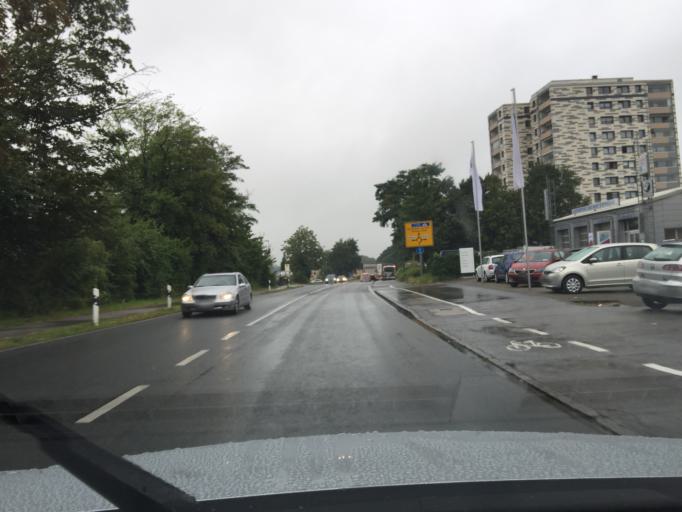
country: DE
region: North Rhine-Westphalia
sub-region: Regierungsbezirk Dusseldorf
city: Heiligenhaus
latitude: 51.3252
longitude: 6.9454
